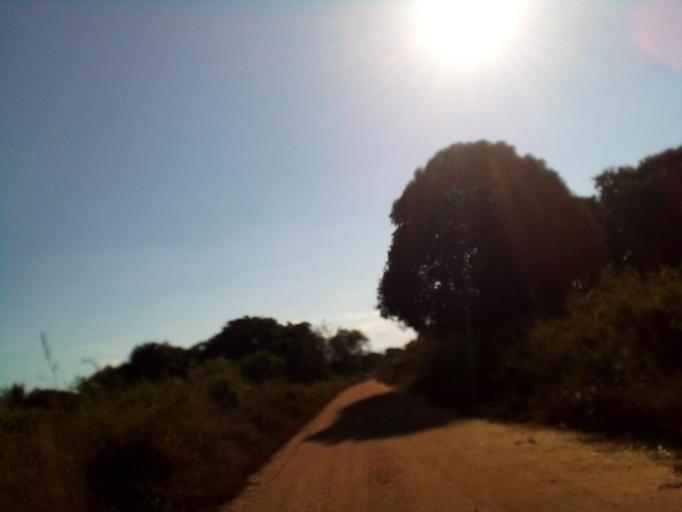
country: MZ
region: Zambezia
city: Quelimane
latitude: -17.5123
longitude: 36.6001
